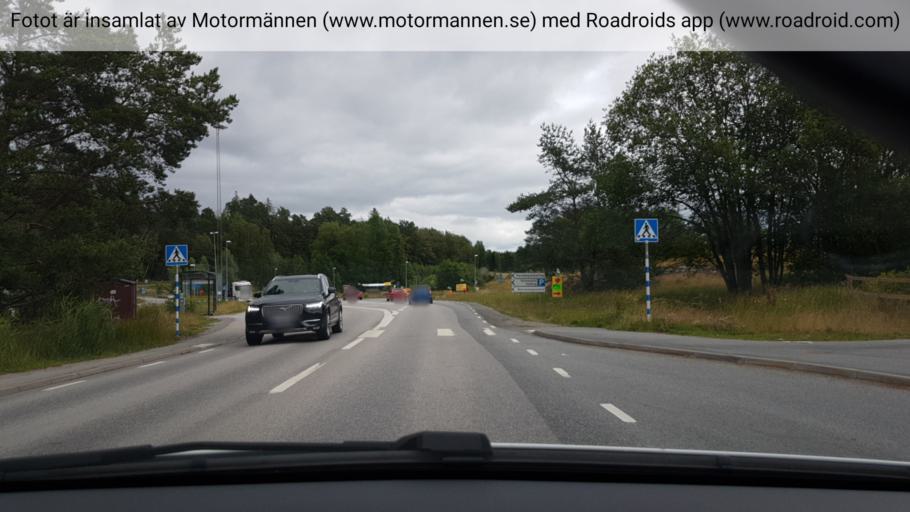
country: SE
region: Stockholm
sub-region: Varmdo Kommun
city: Hemmesta
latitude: 59.3261
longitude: 18.5025
